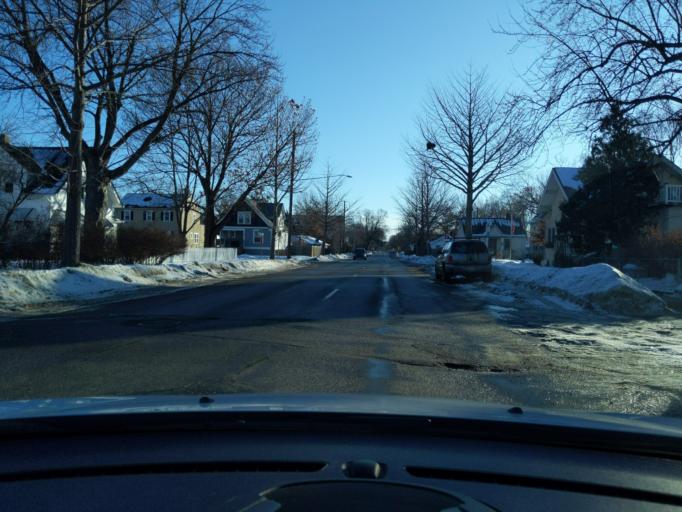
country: US
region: Minnesota
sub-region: Hennepin County
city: Minneapolis
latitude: 44.9270
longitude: -93.2161
